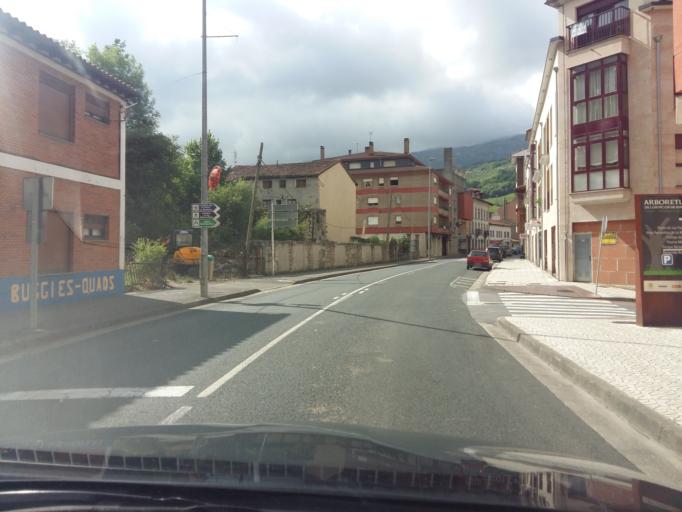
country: ES
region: Cantabria
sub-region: Provincia de Cantabria
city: Tresviso
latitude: 43.3258
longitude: -4.5841
